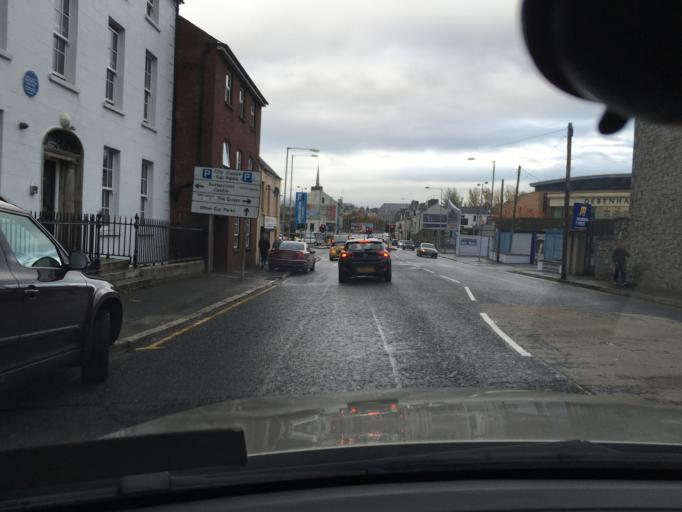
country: GB
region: Northern Ireland
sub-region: Newry and Mourne District
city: Newry
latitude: 54.1694
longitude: -6.3424
